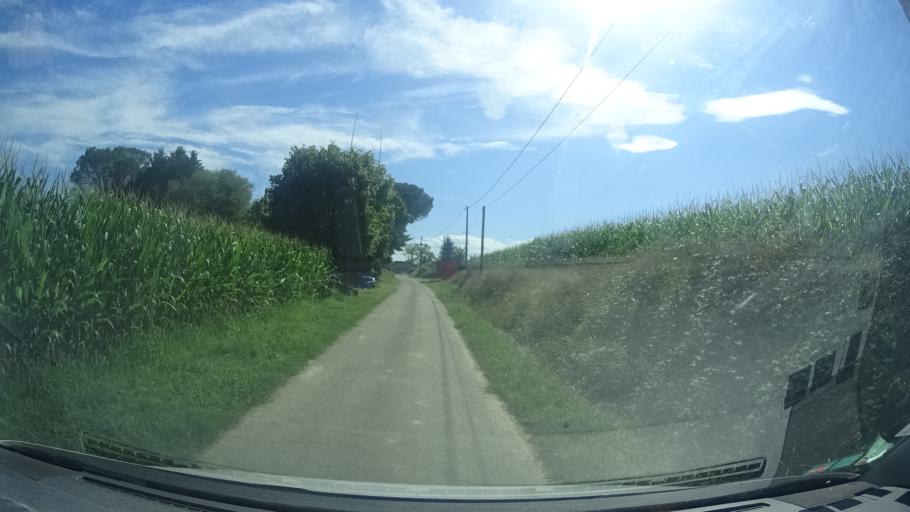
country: FR
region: Aquitaine
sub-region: Departement des Pyrenees-Atlantiques
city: Orthez
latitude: 43.4933
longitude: -0.7101
